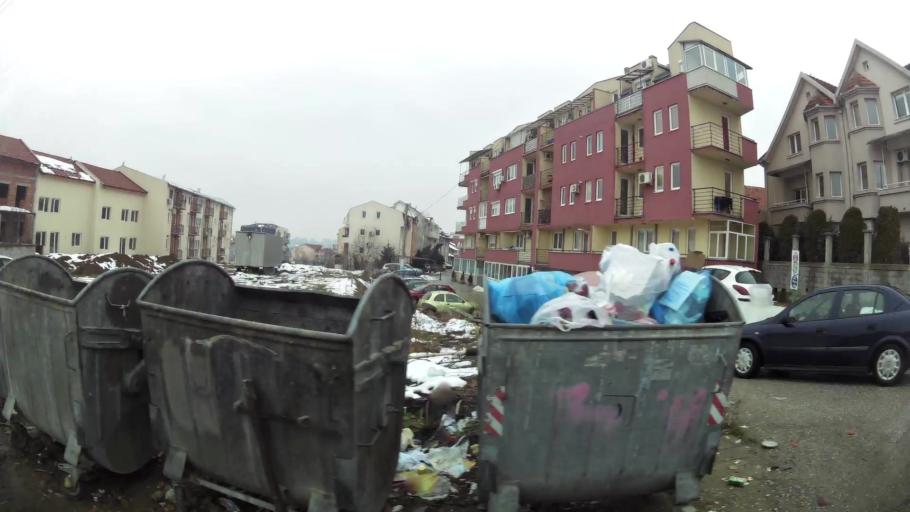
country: RS
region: Central Serbia
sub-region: Belgrade
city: Vozdovac
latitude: 44.7598
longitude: 20.5028
